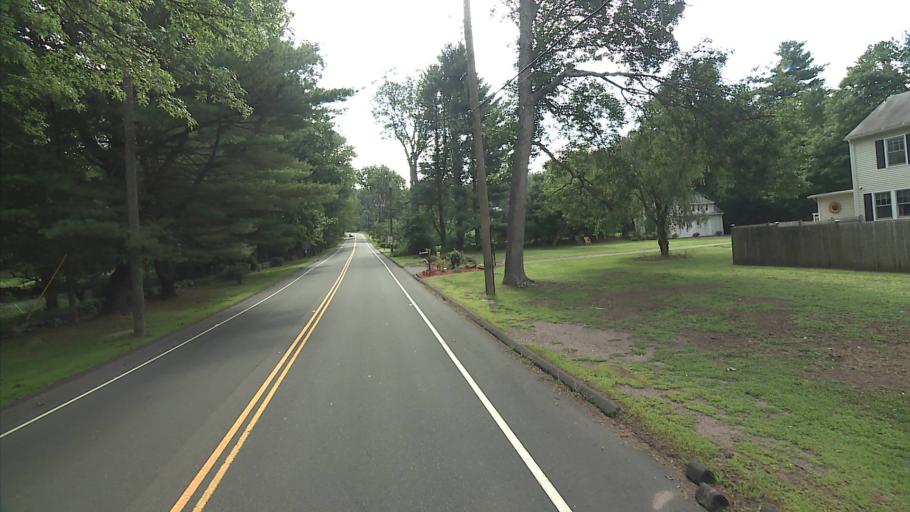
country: US
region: Connecticut
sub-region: New Haven County
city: Woodbridge
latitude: 41.3288
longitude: -73.0245
